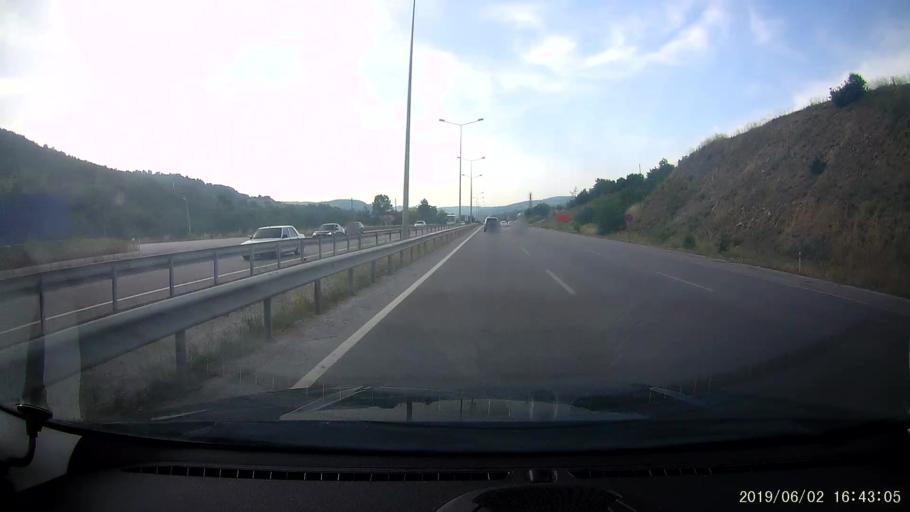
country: TR
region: Samsun
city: Kavak
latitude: 41.1292
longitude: 36.1345
